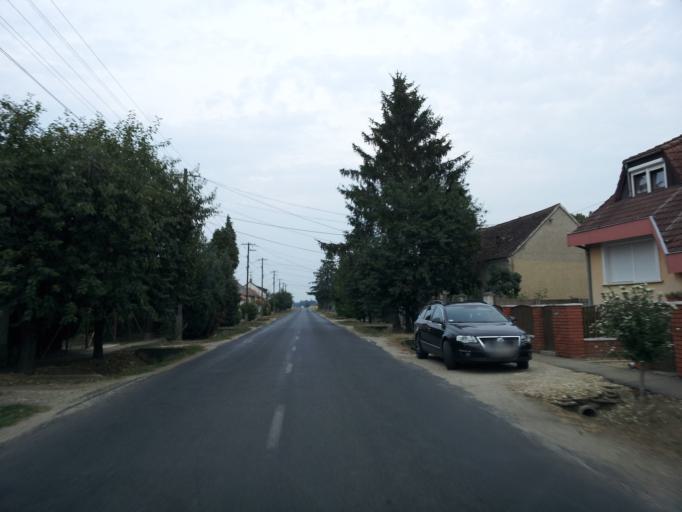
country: HU
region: Vas
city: Vep
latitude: 47.2043
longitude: 16.7922
